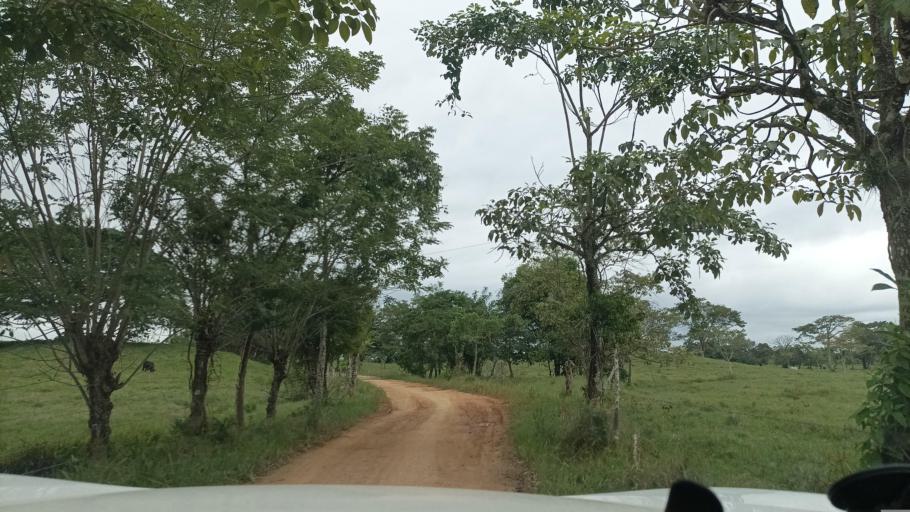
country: MX
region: Veracruz
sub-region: Uxpanapa
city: Poblado Cinco
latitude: 17.5074
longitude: -94.5626
